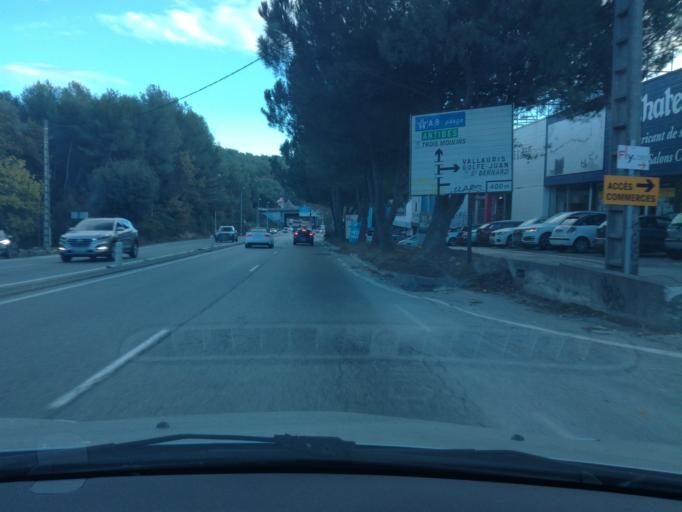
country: FR
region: Provence-Alpes-Cote d'Azur
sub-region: Departement des Alpes-Maritimes
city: Vallauris
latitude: 43.6050
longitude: 7.0603
